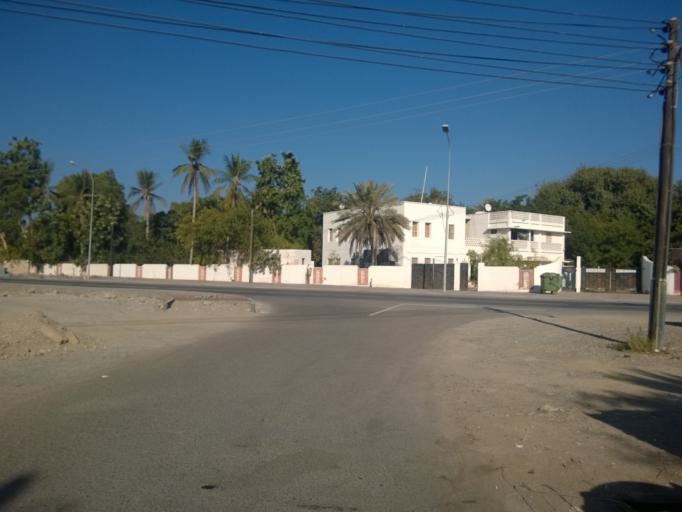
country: OM
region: Muhafazat Masqat
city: As Sib al Jadidah
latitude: 23.6689
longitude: 58.1873
